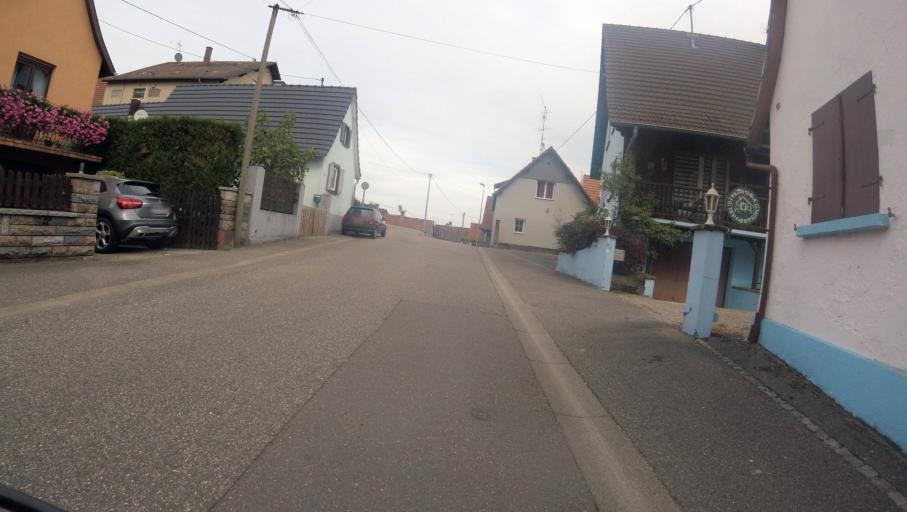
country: DE
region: Baden-Wuerttemberg
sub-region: Karlsruhe Region
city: Steinmauern
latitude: 48.9298
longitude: 8.1553
